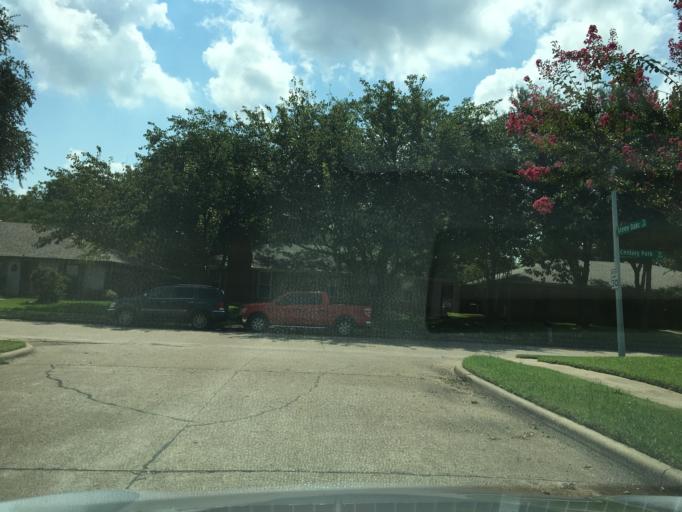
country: US
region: Texas
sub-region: Dallas County
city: Garland
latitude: 32.9461
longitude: -96.6402
